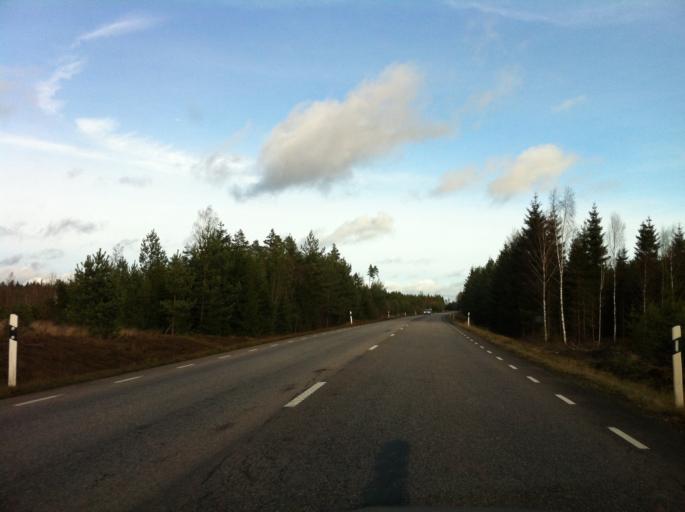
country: SE
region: Kronoberg
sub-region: Almhults Kommun
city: AElmhult
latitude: 56.5952
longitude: 14.2099
